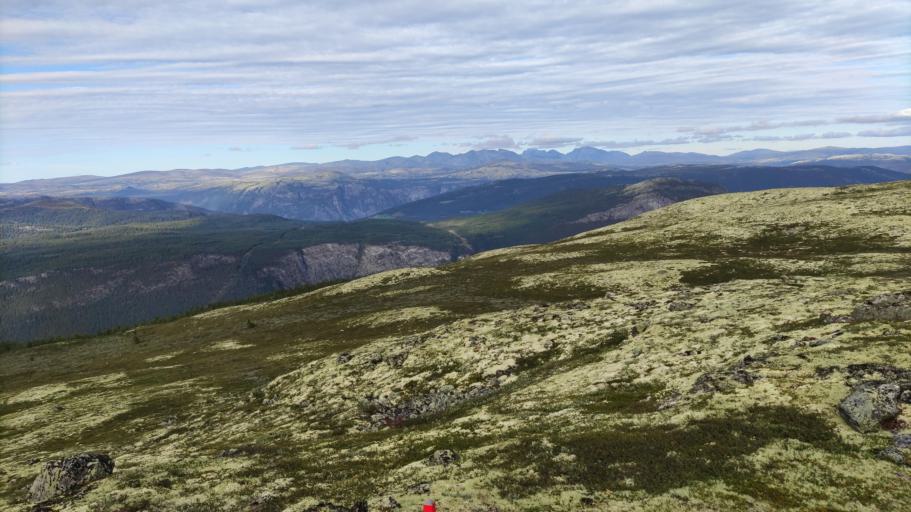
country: NO
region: Oppland
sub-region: Dovre
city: Dovre
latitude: 61.7817
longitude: 9.2864
